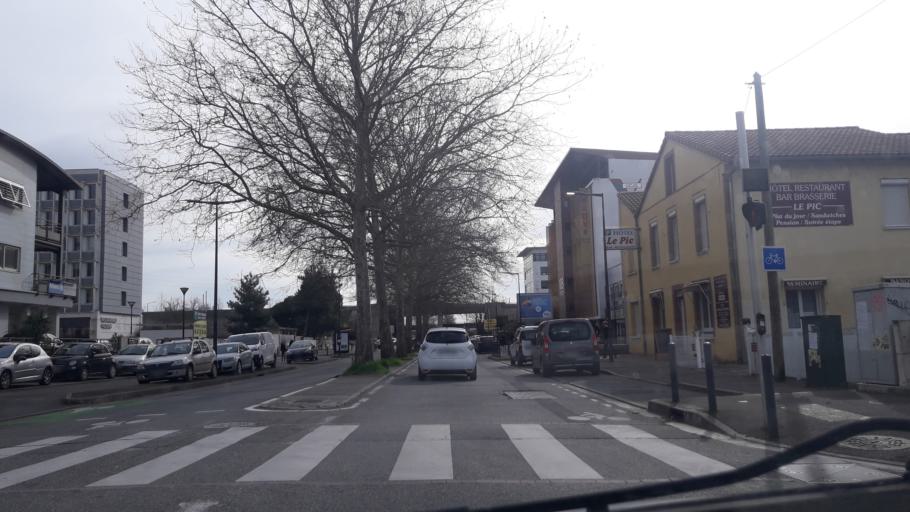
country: FR
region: Midi-Pyrenees
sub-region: Departement de la Haute-Garonne
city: Toulouse
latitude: 43.5722
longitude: 1.4243
